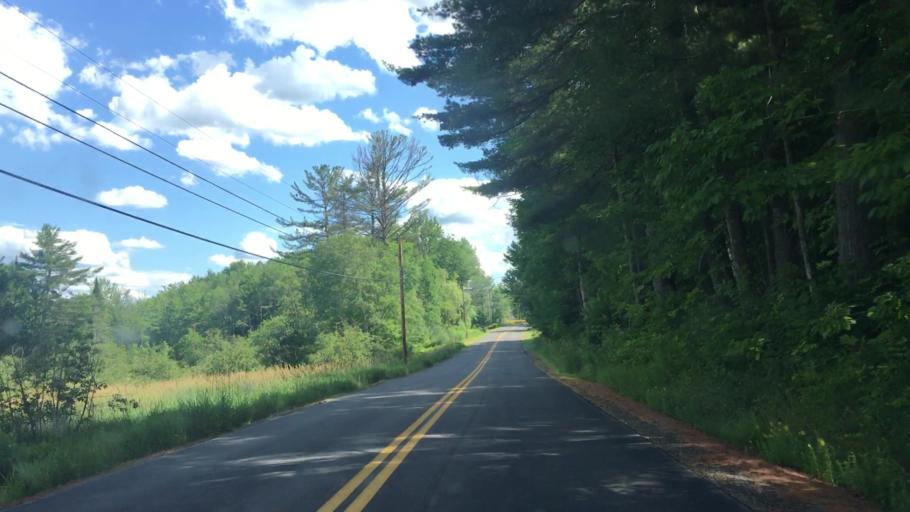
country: US
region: Maine
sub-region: Franklin County
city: Farmington
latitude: 44.6788
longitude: -70.1319
